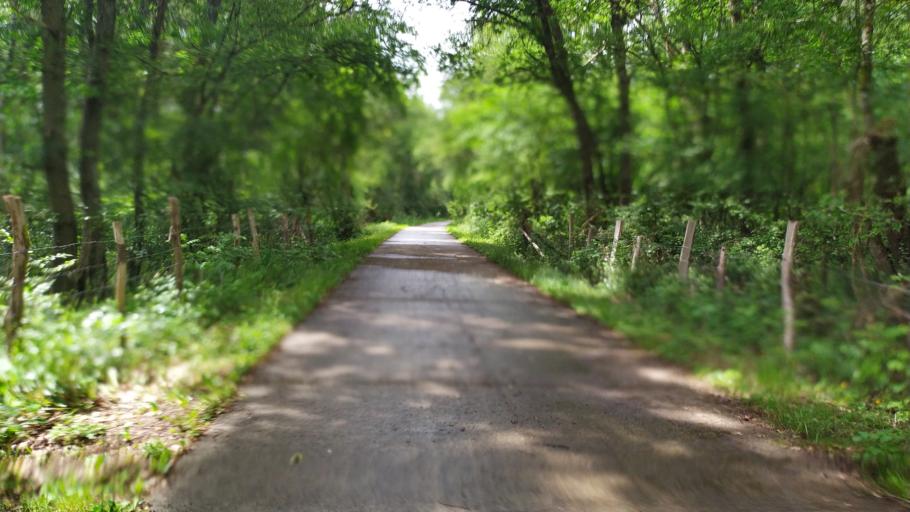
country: BE
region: Wallonia
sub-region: Province du Luxembourg
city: Wellin
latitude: 50.1487
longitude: 5.1438
